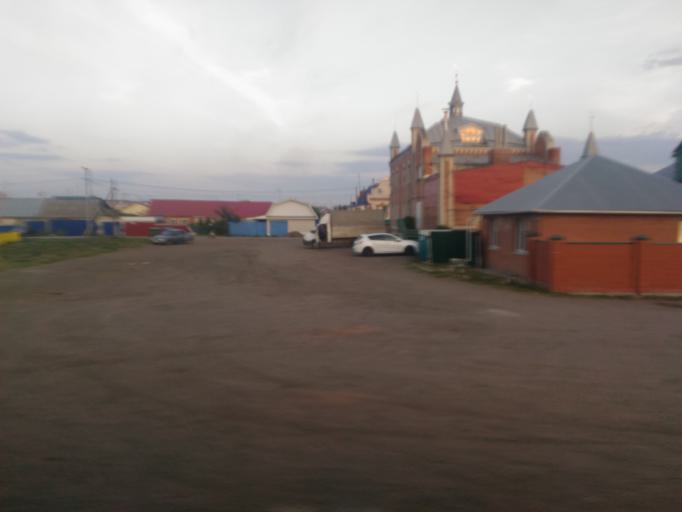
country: RU
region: Ulyanovsk
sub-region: Ulyanovskiy Rayon
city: Ulyanovsk
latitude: 54.2649
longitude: 48.2816
